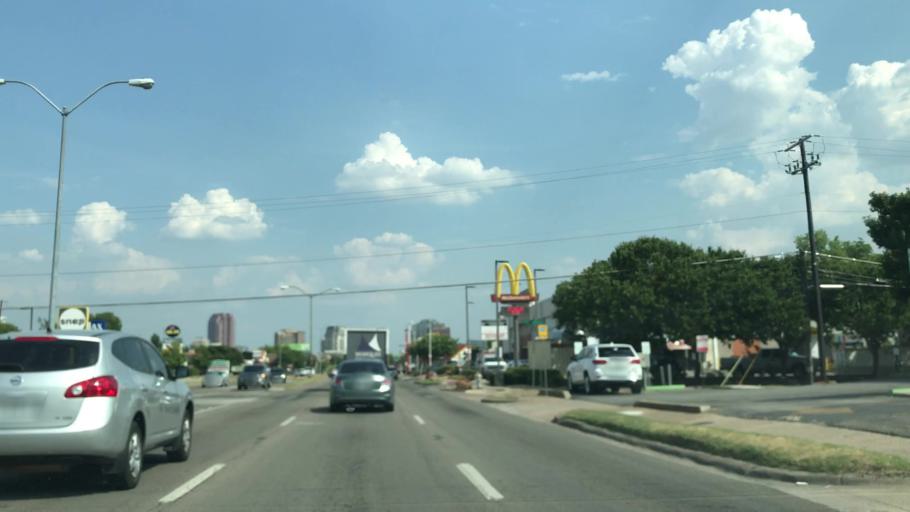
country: US
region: Texas
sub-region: Dallas County
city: Highland Park
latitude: 32.8192
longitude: -96.8142
